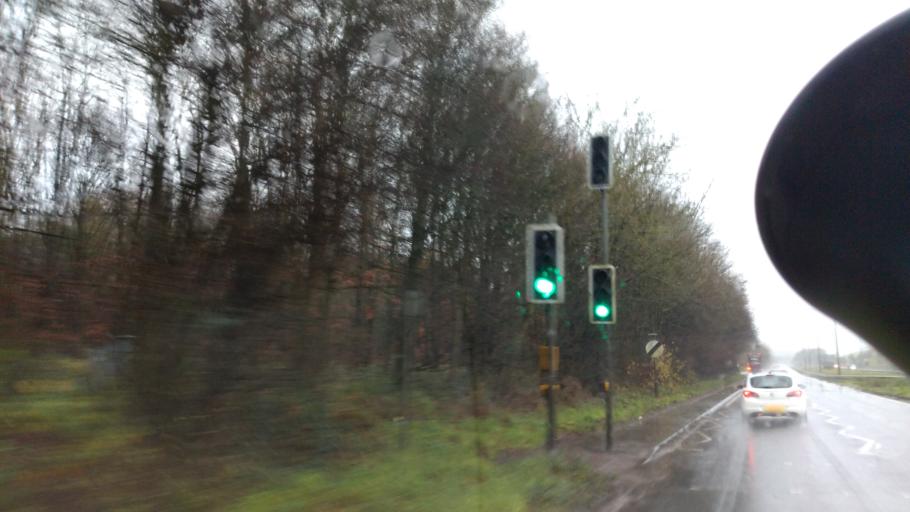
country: GB
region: England
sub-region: East Sussex
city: Lewes
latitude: 50.8668
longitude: -0.0238
